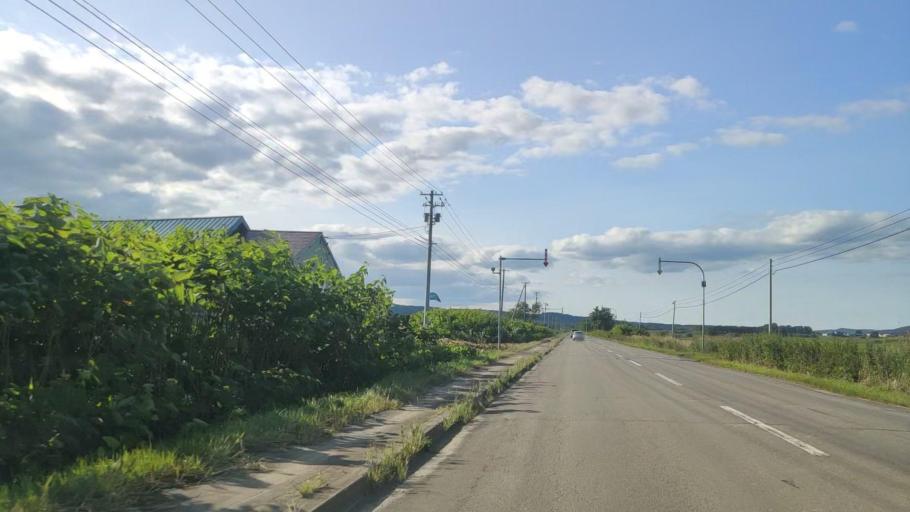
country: JP
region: Hokkaido
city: Makubetsu
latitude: 44.8249
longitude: 142.0640
